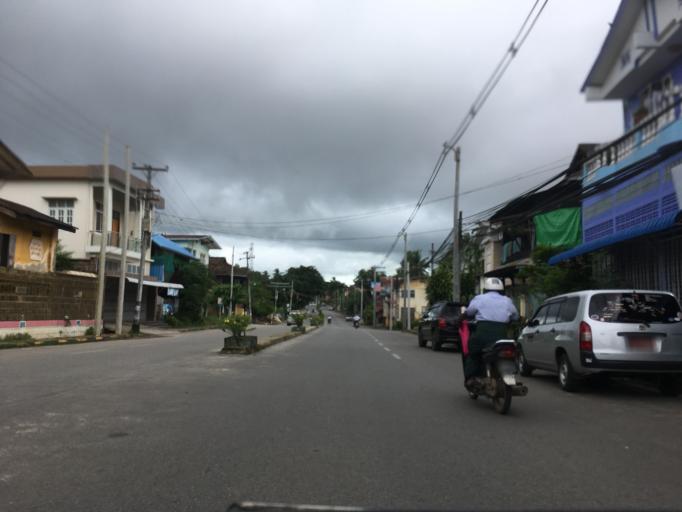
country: MM
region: Mon
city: Mawlamyine
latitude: 16.4737
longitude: 97.6227
